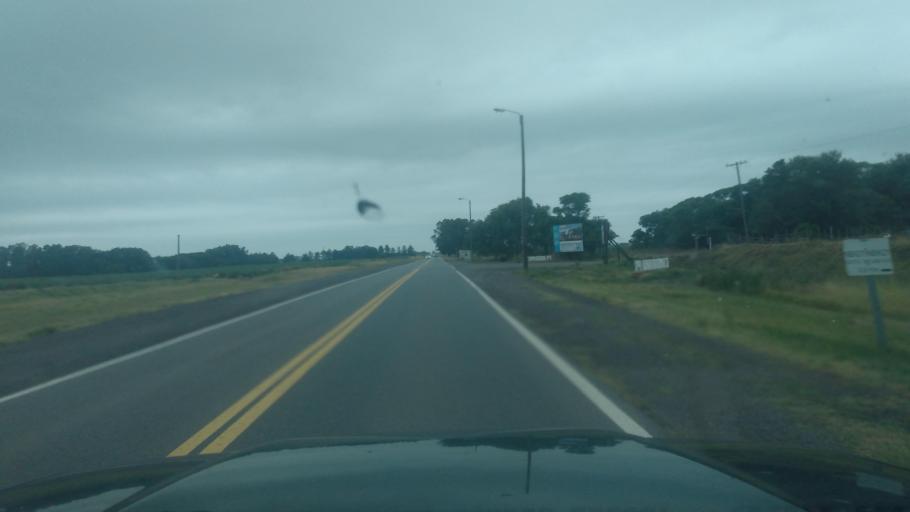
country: AR
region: Buenos Aires
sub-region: Partido de Bragado
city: Bragado
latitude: -35.2766
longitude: -60.5868
